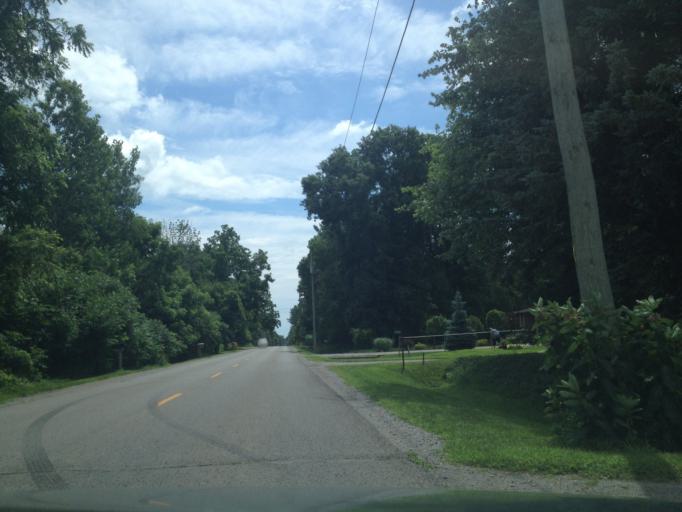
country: CA
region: Ontario
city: Norfolk County
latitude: 42.8076
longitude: -80.3184
